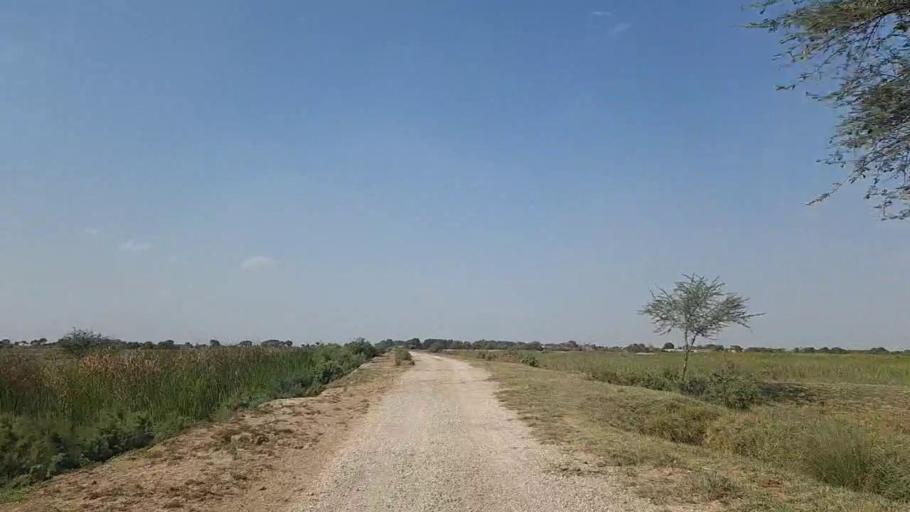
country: PK
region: Sindh
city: Jati
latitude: 24.5144
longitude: 68.2946
